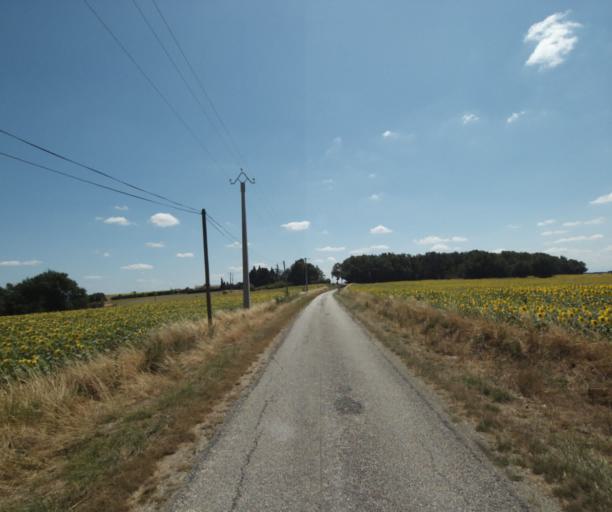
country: FR
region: Midi-Pyrenees
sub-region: Departement de la Haute-Garonne
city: Saint-Felix-Lauragais
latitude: 43.4762
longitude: 1.8685
